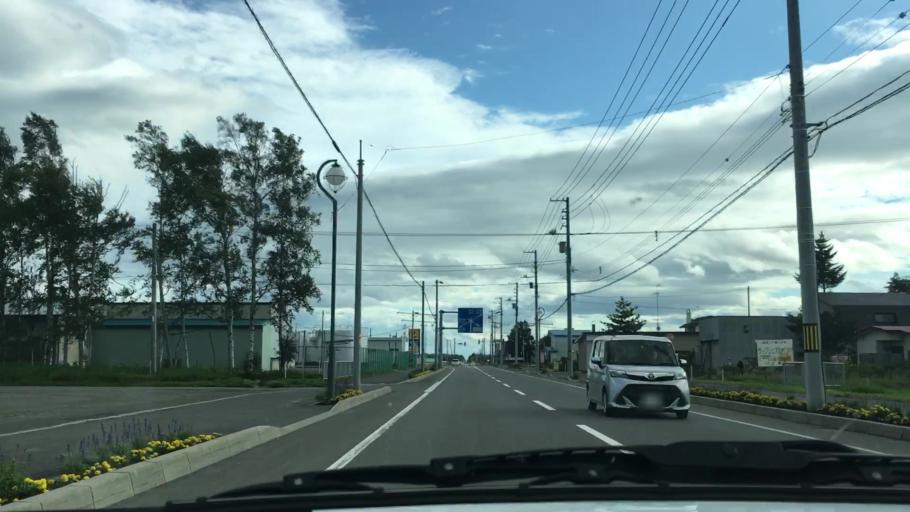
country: JP
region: Hokkaido
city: Otofuke
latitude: 43.2270
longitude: 143.2938
